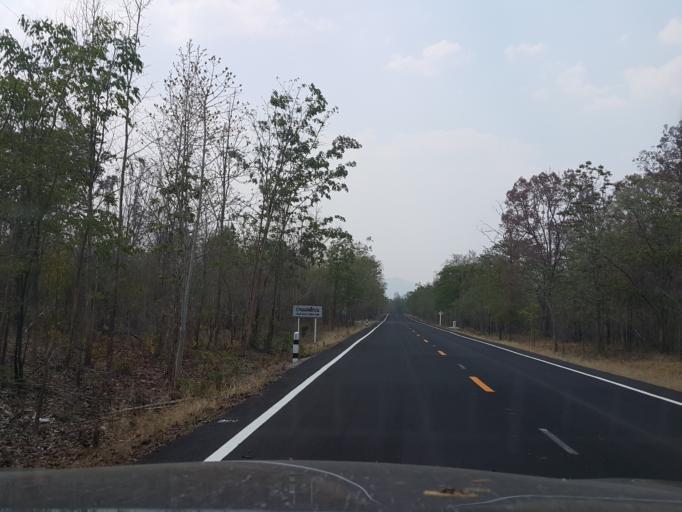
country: TH
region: Lampang
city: Mae Phrik
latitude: 17.4814
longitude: 99.1091
